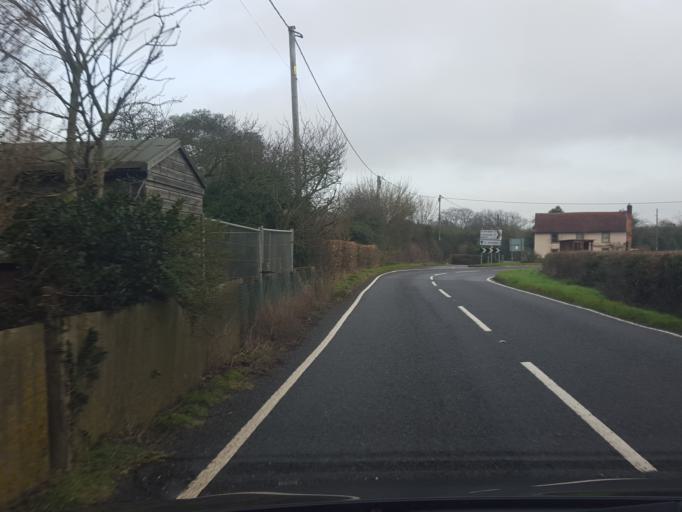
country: GB
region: England
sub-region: Essex
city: West Bergholt
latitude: 51.9490
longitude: 0.8191
